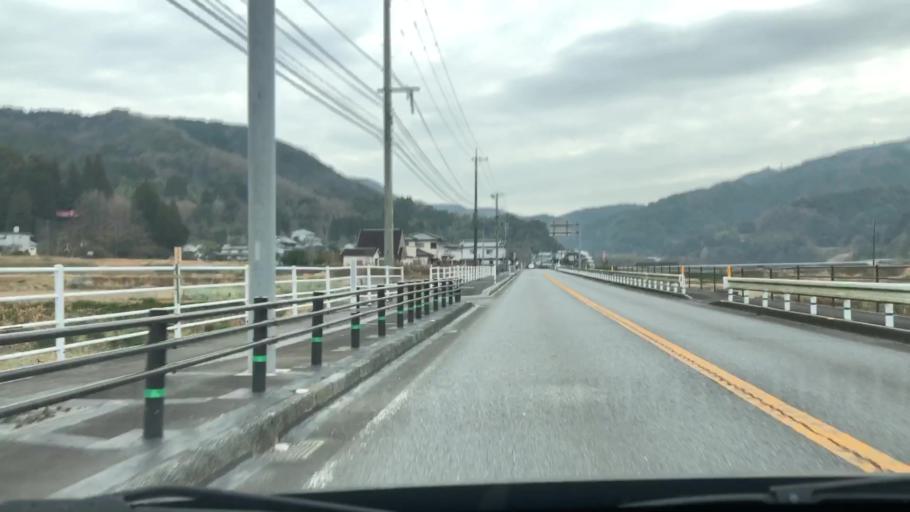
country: JP
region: Oita
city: Usuki
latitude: 33.0062
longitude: 131.7207
